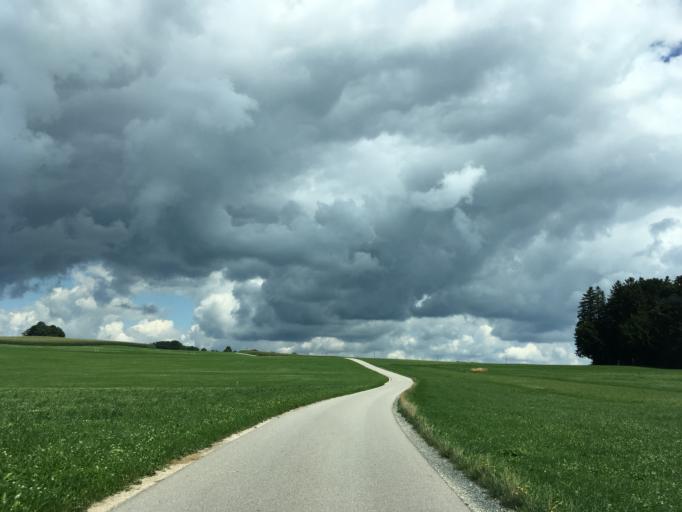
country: DE
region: Bavaria
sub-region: Upper Bavaria
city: Amerang
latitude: 47.9895
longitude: 12.3403
